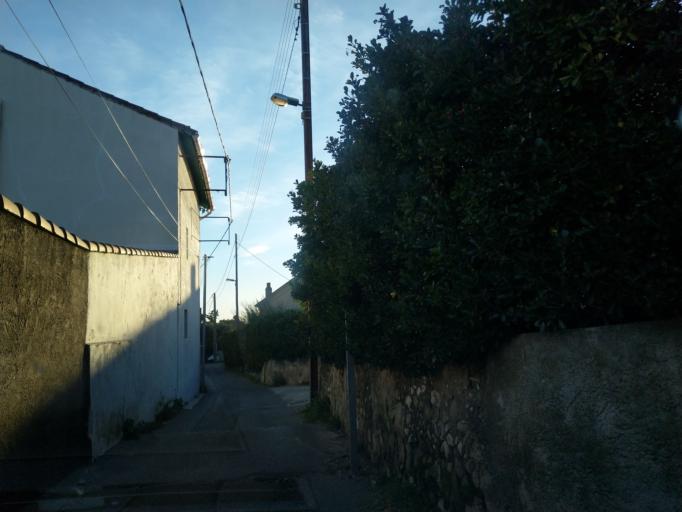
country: FR
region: Provence-Alpes-Cote d'Azur
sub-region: Departement des Bouches-du-Rhone
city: Plan-de-Cuques
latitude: 43.3478
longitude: 5.4534
